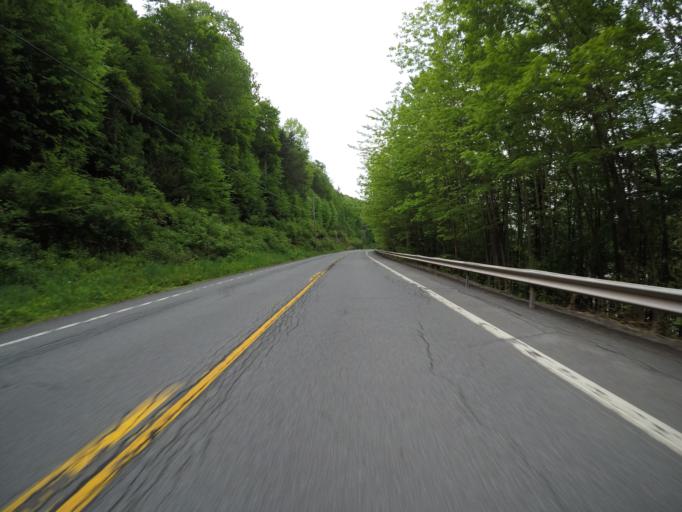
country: US
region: New York
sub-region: Delaware County
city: Delhi
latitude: 42.0778
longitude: -74.9409
